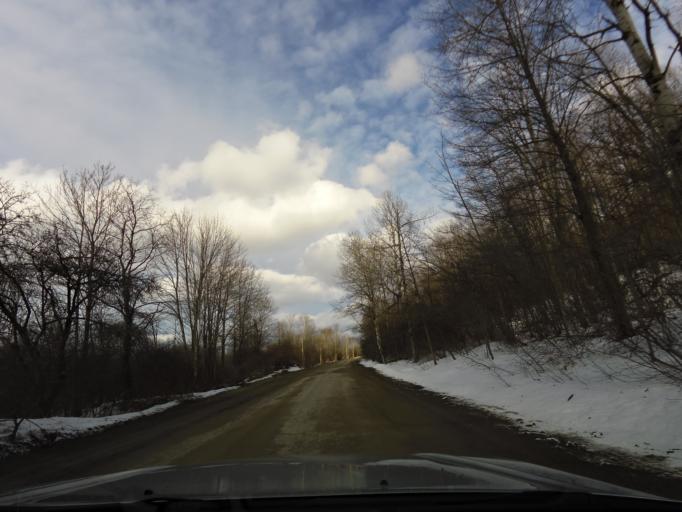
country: US
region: New York
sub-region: Cattaraugus County
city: Franklinville
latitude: 42.3399
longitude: -78.4377
